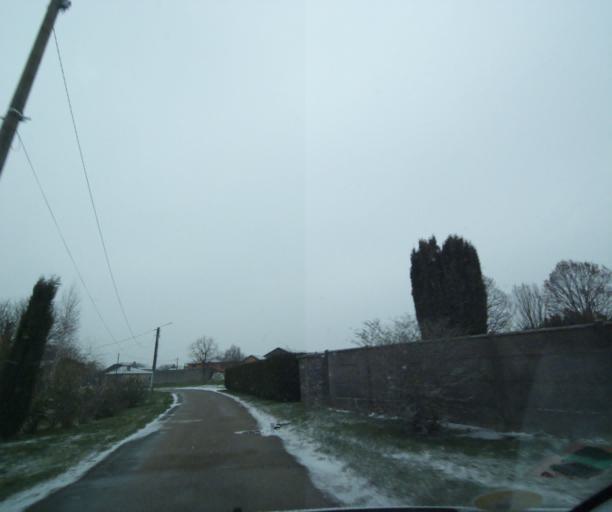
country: FR
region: Champagne-Ardenne
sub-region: Departement de la Haute-Marne
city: Wassy
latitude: 48.4695
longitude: 4.9953
